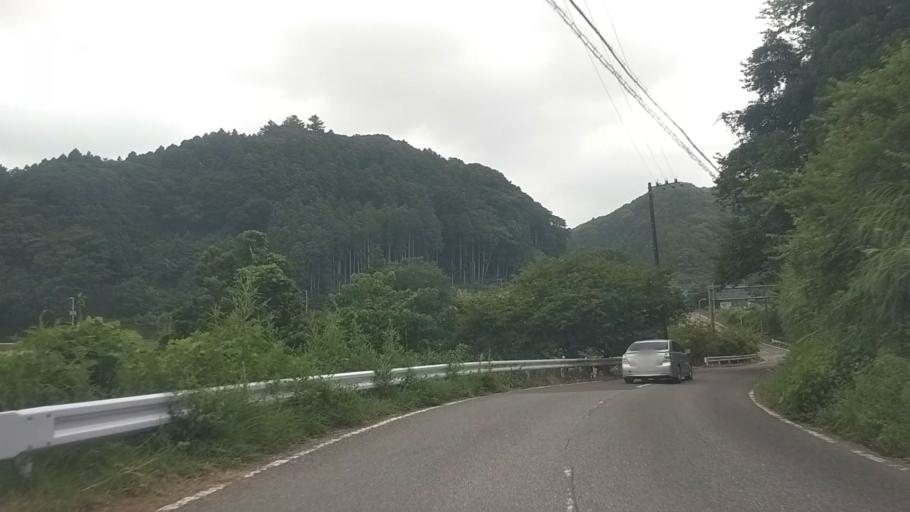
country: JP
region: Chiba
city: Kawaguchi
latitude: 35.2173
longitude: 140.1363
